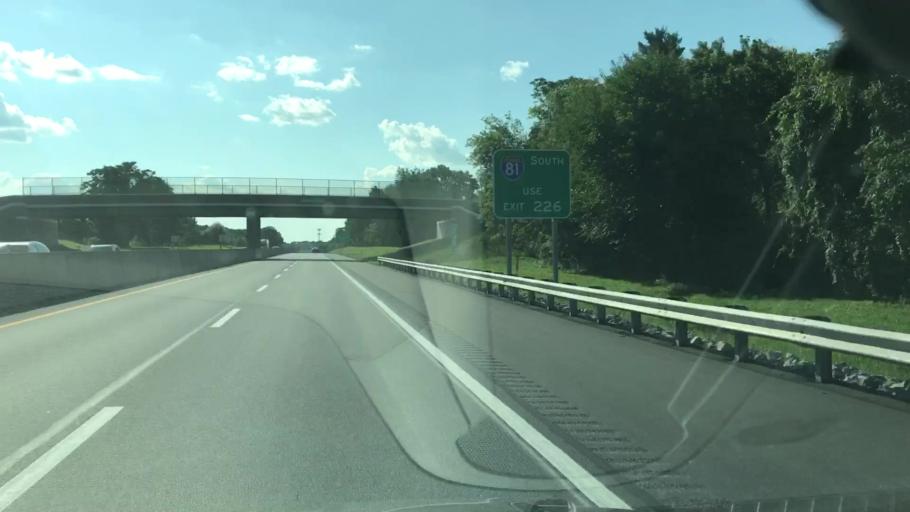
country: US
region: Pennsylvania
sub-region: Dauphin County
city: Highspire
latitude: 40.2135
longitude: -76.7705
